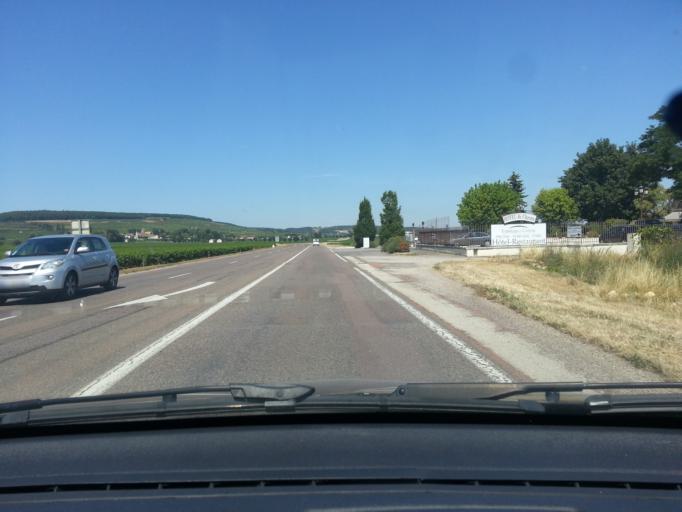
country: FR
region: Bourgogne
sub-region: Departement de la Cote-d'Or
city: Beaune
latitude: 47.0519
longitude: 4.8566
